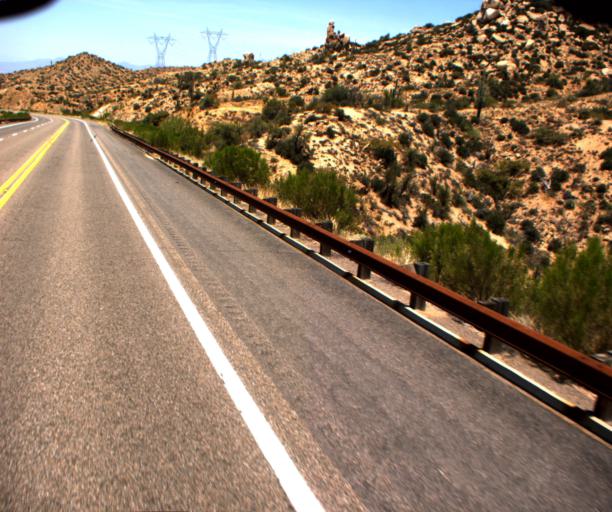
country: US
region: Arizona
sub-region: Gila County
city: Miami
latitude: 33.5426
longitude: -110.9385
